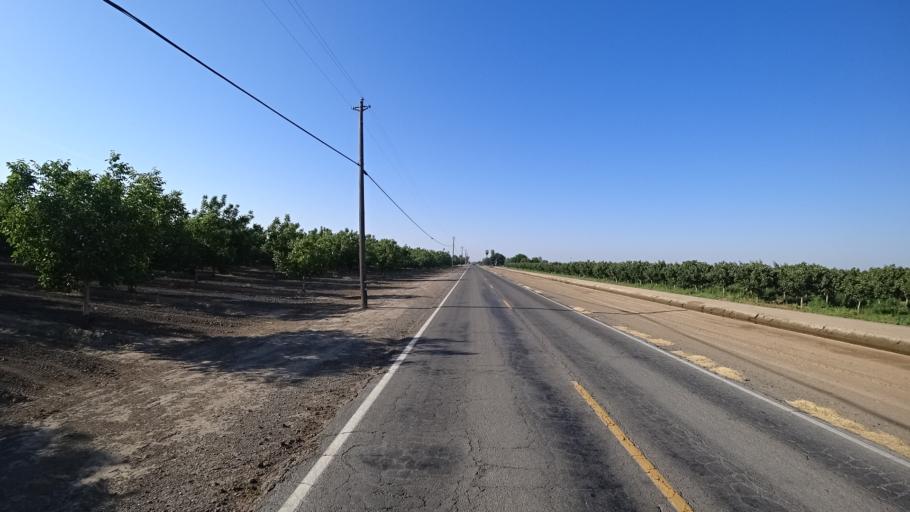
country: US
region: California
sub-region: Kings County
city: Armona
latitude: 36.2668
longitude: -119.7090
